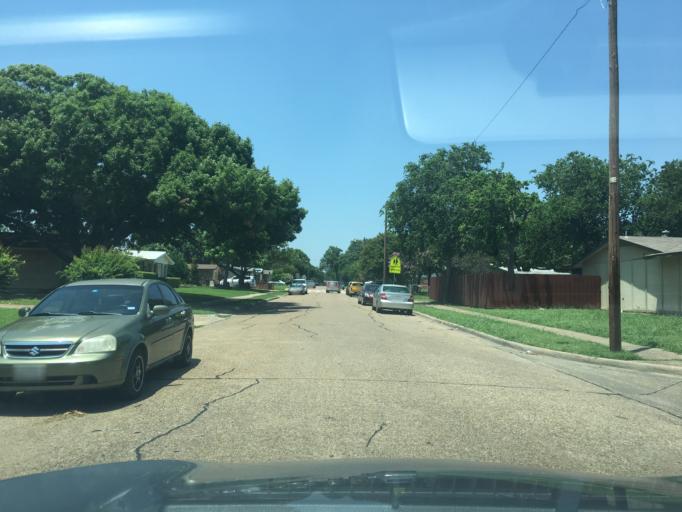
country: US
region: Texas
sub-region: Dallas County
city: Richardson
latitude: 32.9207
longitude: -96.7052
